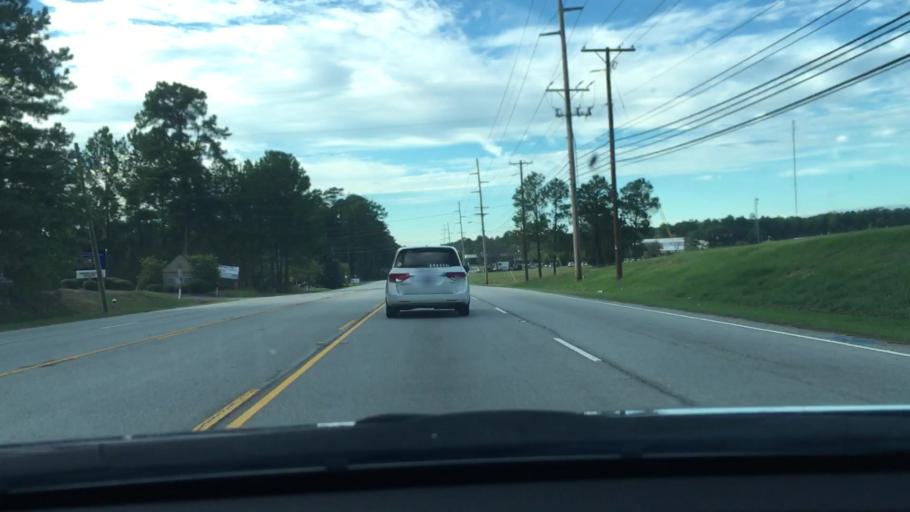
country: US
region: South Carolina
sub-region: Lexington County
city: Saint Andrews
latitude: 34.0728
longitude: -81.1224
